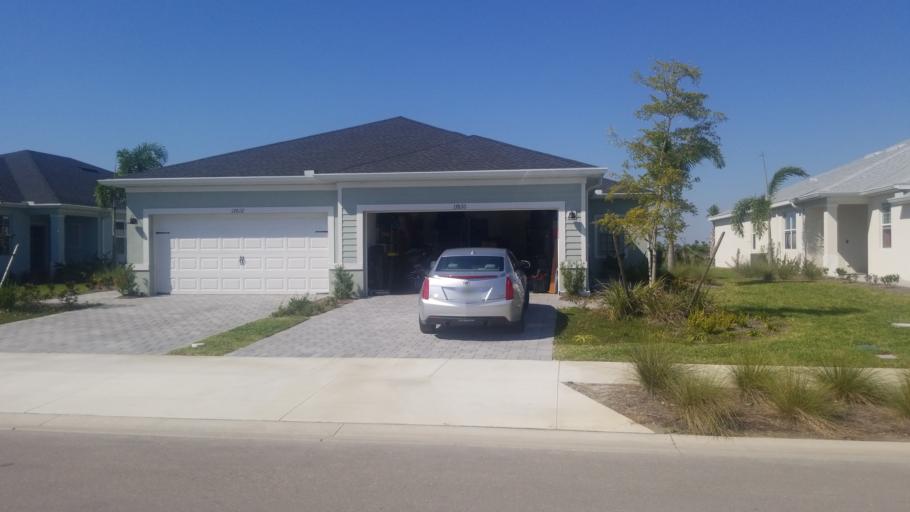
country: US
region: Florida
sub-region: Lee County
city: Olga
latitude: 26.7794
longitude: -81.7398
